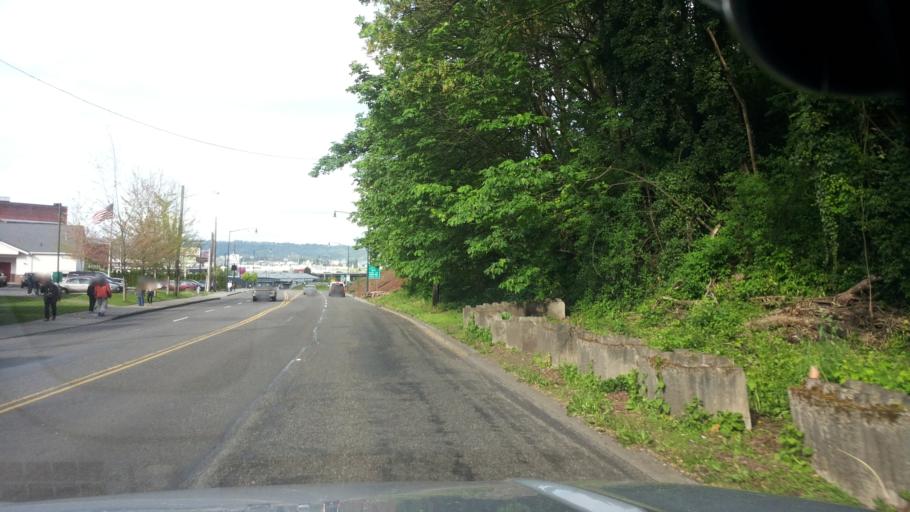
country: US
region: Washington
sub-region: Pierce County
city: Tacoma
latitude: 47.2350
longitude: -122.4395
